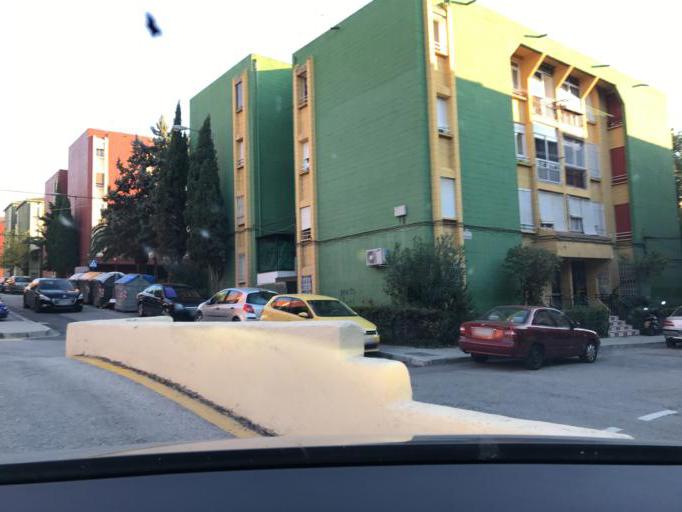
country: ES
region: Andalusia
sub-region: Provincia de Granada
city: Granada
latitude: 37.1988
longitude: -3.5989
